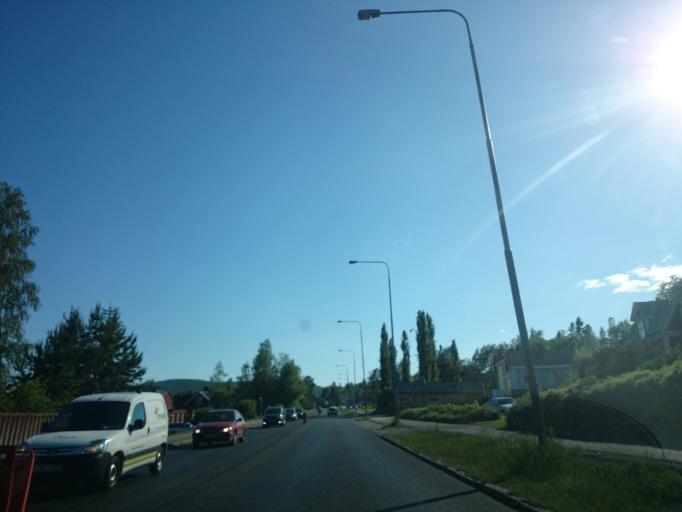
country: SE
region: Vaesternorrland
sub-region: Haernoesands Kommun
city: Haernoesand
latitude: 62.6220
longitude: 17.9174
